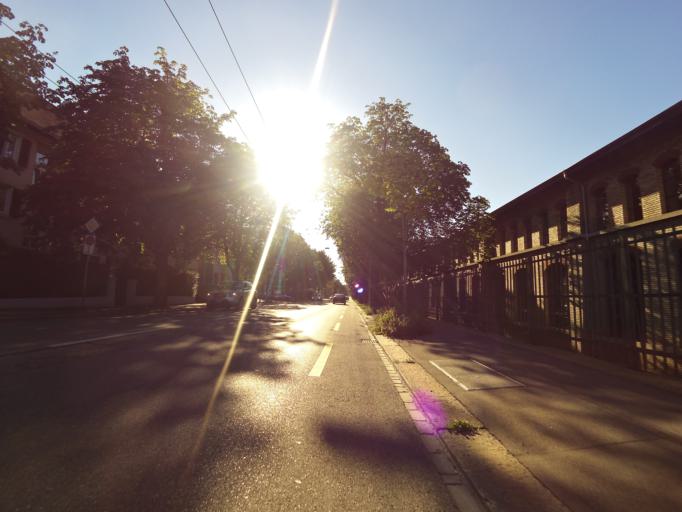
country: CH
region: Zurich
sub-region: Bezirk Zuerich
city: Zuerich (Kreis 4) / Hard
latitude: 47.3862
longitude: 8.5048
